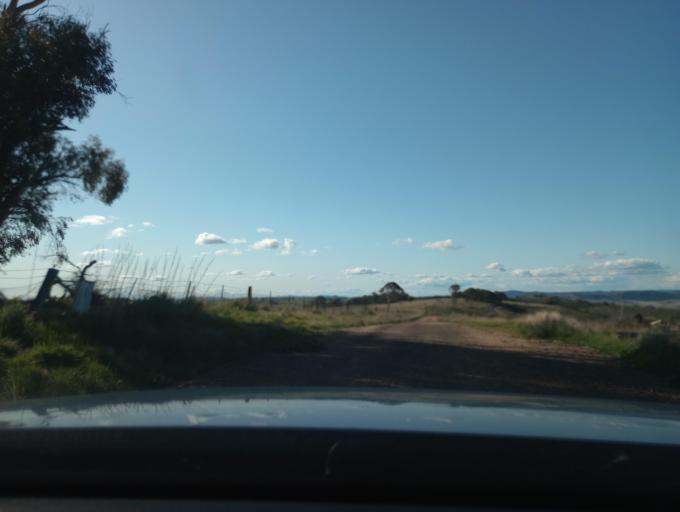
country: AU
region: New South Wales
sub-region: Blayney
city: Blayney
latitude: -33.4259
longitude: 149.3141
